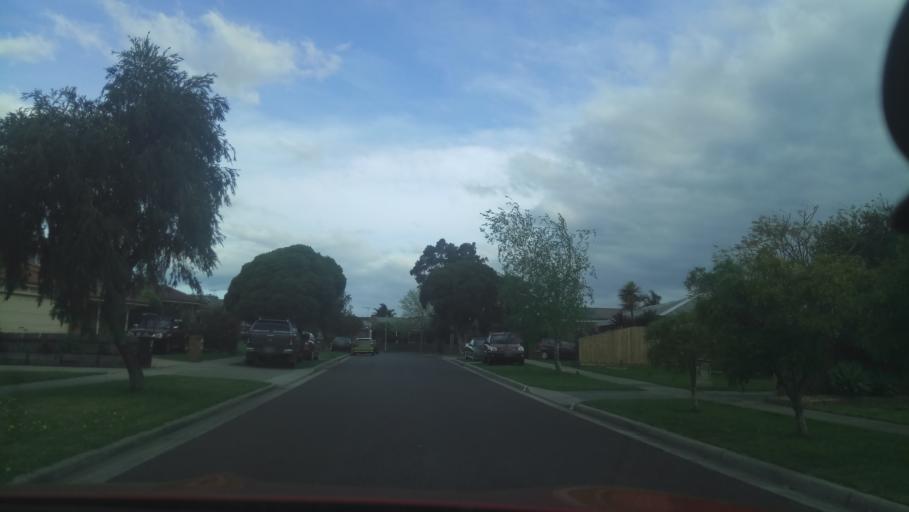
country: AU
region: Victoria
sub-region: Casey
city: Cranbourne North
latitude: -38.0677
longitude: 145.2724
